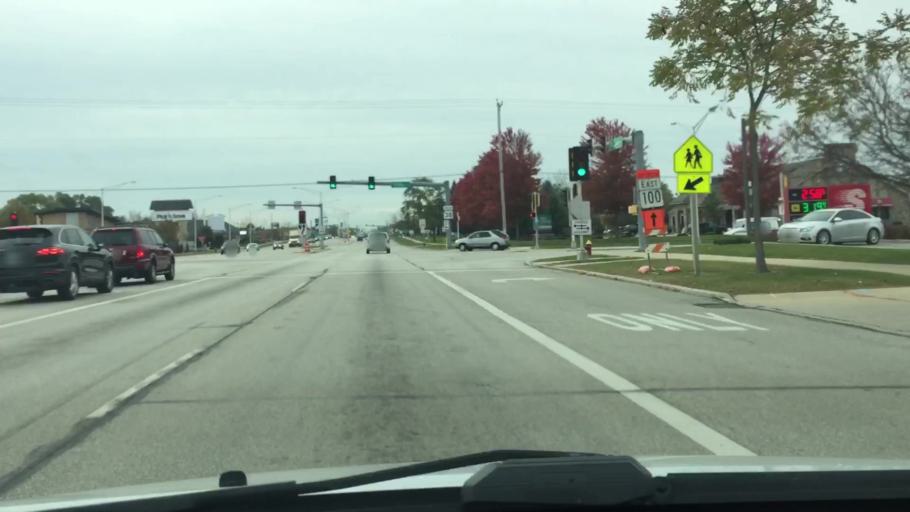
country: US
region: Wisconsin
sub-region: Milwaukee County
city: Oak Creek
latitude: 42.8871
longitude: -87.9123
